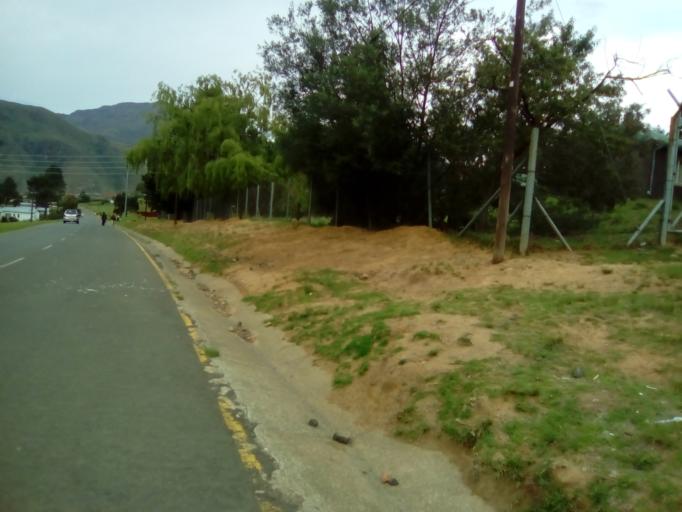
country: LS
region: Qacha's Nek
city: Qacha's Nek
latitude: -30.1125
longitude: 28.6810
